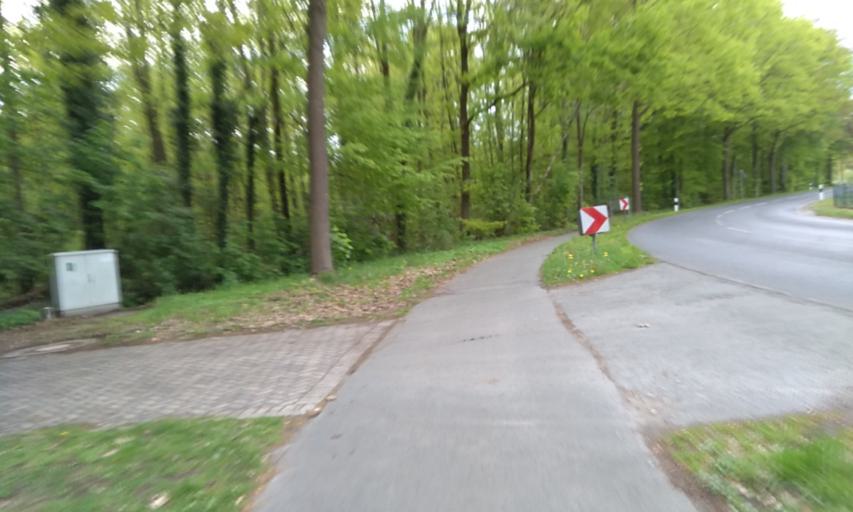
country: DE
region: Lower Saxony
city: Wohnste
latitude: 53.3891
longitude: 9.5396
